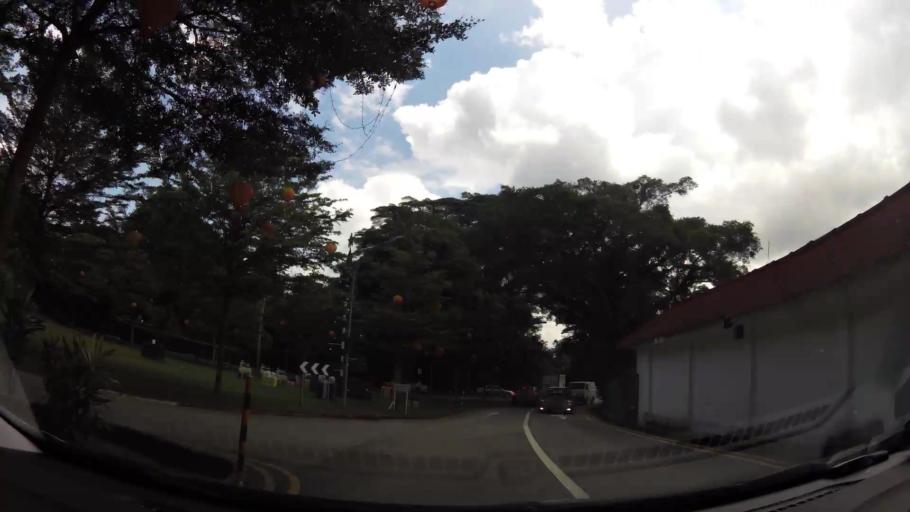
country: SG
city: Singapore
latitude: 1.3039
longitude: 103.8107
